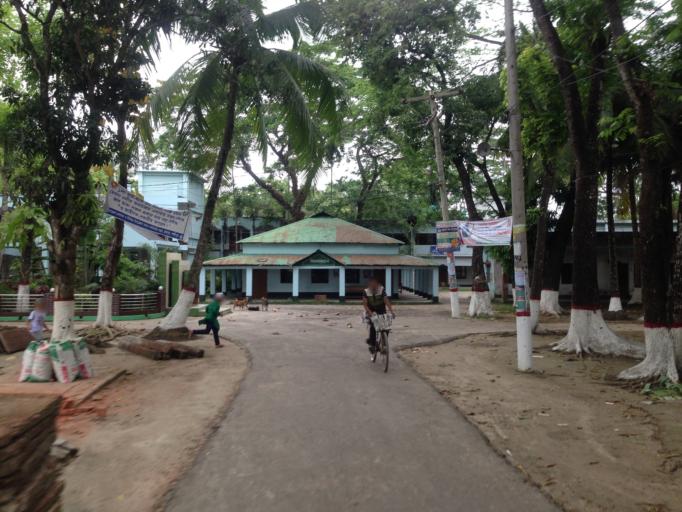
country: BD
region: Chittagong
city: Raipur
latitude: 23.0362
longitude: 90.7614
